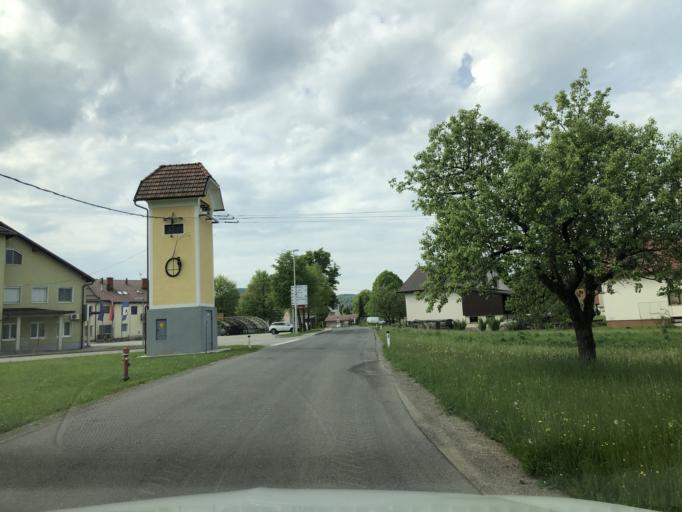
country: SI
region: Bloke
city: Nova Vas
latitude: 45.7745
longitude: 14.5059
